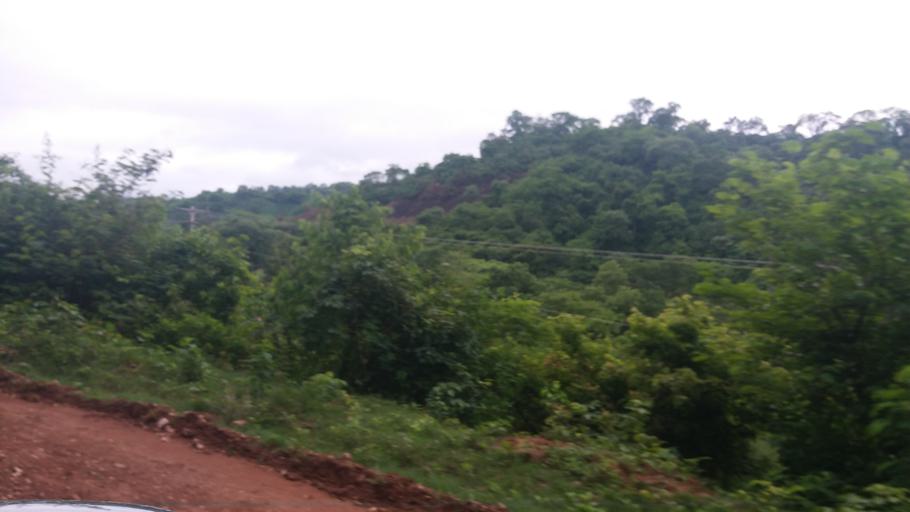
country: BO
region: Tarija
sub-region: Provincia Gran Chaco
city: Yacuiba
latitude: -21.8313
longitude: -63.7195
